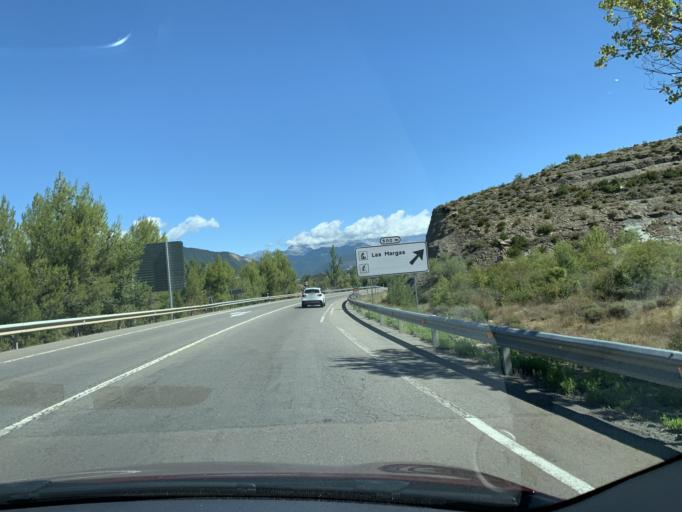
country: ES
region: Aragon
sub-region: Provincia de Huesca
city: Sabinanigo
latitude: 42.5079
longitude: -0.3535
